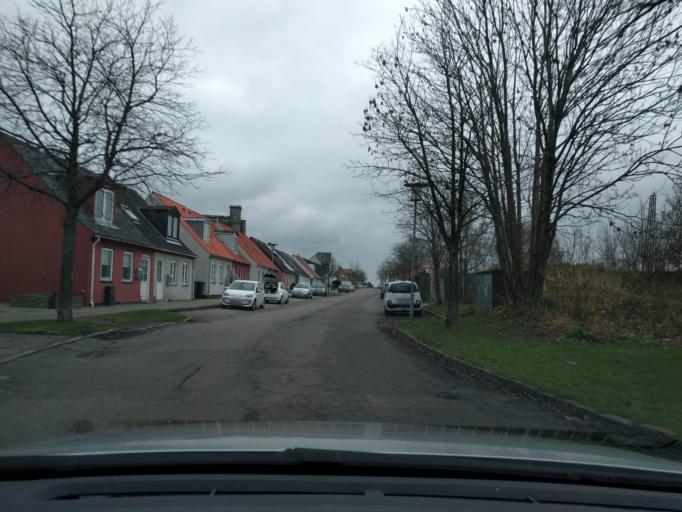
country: DK
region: Zealand
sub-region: Guldborgsund Kommune
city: Nykobing Falster
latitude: 54.7745
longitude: 11.8681
